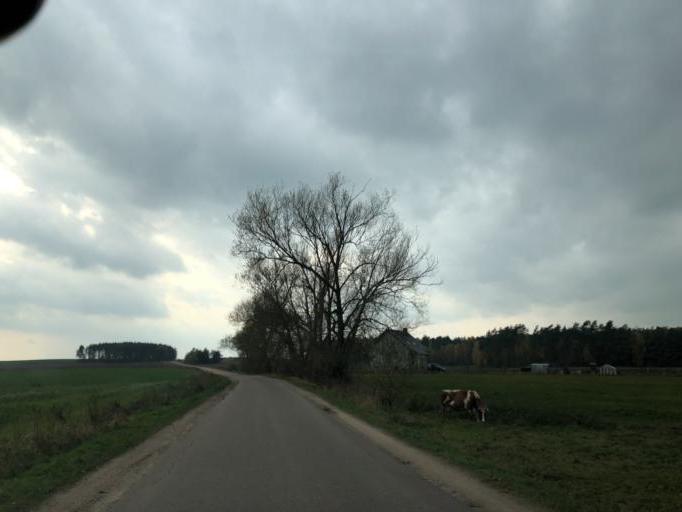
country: PL
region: Podlasie
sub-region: Lomza
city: Lomza
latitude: 53.1531
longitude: 22.0011
